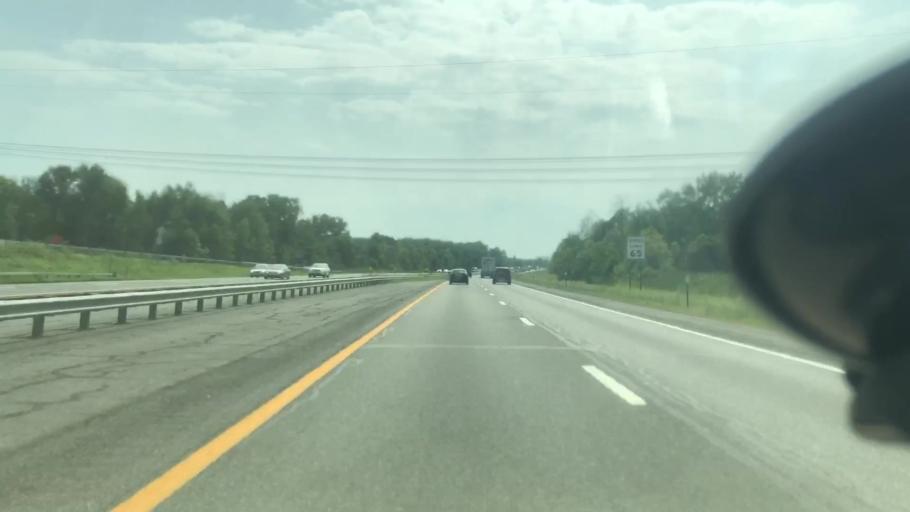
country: US
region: New York
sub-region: Rensselaer County
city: Castleton-on-Hudson
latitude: 42.5133
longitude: -73.7912
